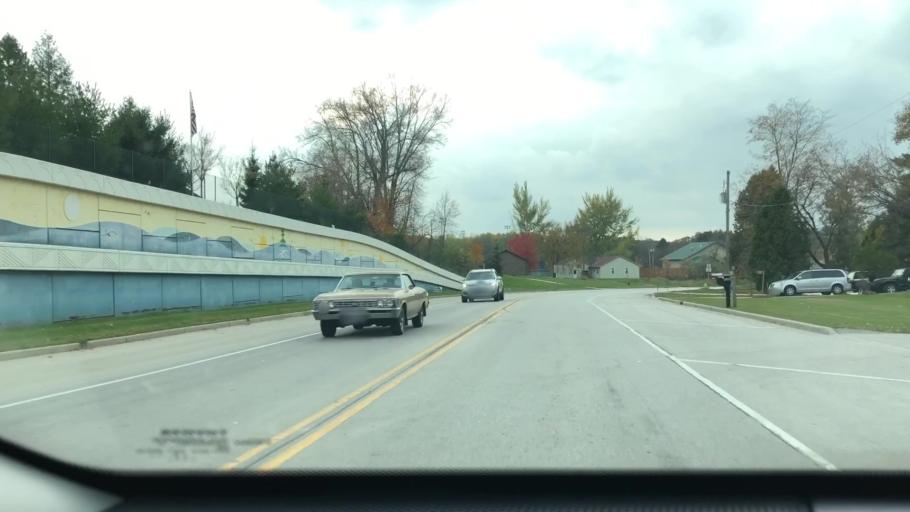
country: US
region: Wisconsin
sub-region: Brown County
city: Oneida
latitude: 44.4990
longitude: -88.1793
